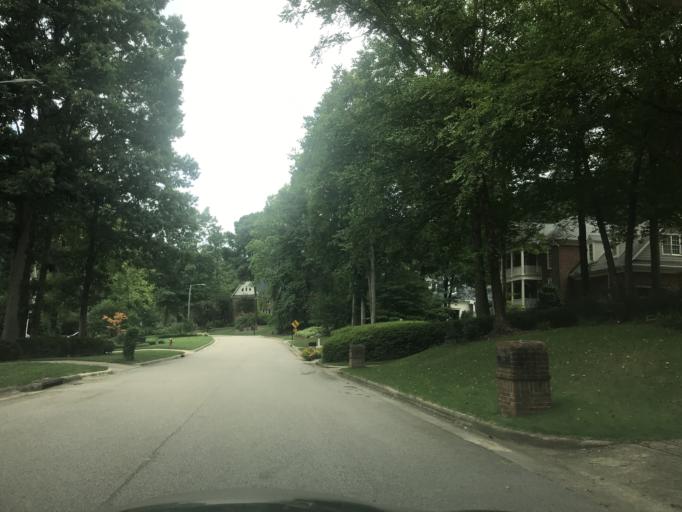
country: US
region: North Carolina
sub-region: Wake County
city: West Raleigh
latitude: 35.8851
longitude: -78.6065
